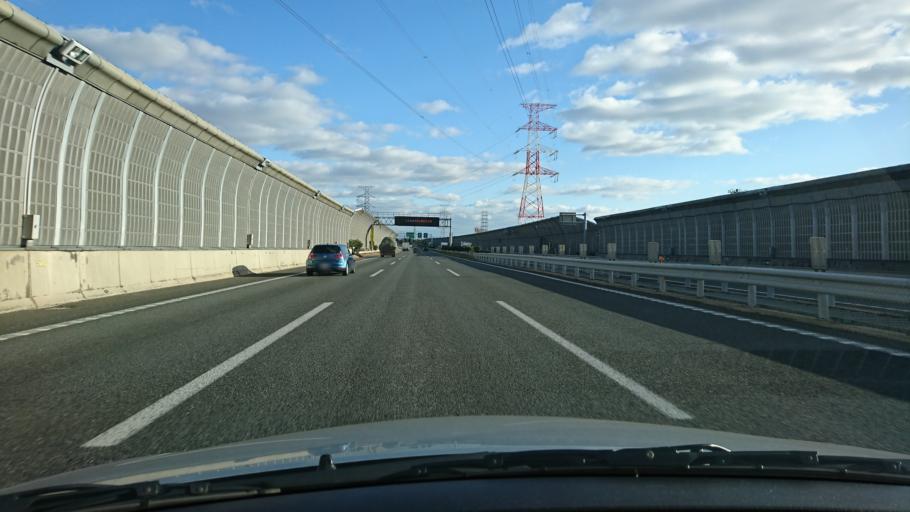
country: JP
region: Hyogo
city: Takarazuka
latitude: 34.8109
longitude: 135.3630
